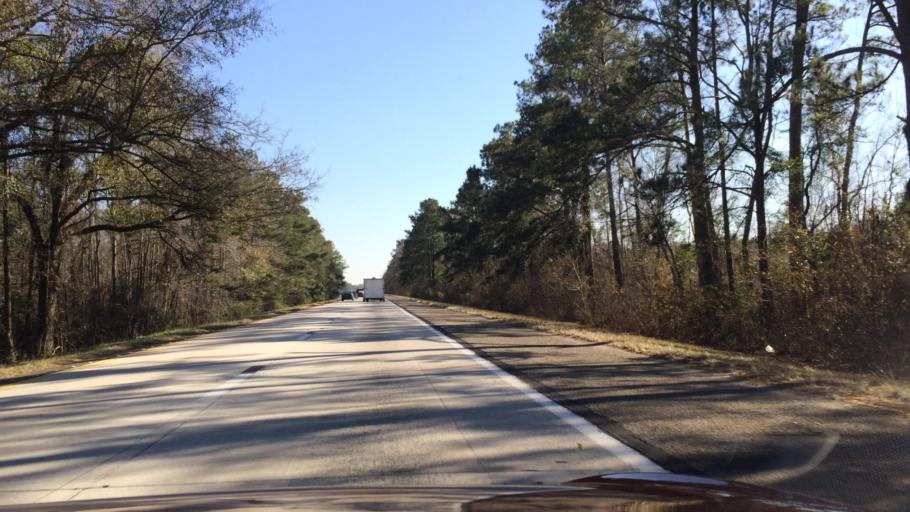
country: US
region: South Carolina
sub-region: Orangeburg County
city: Holly Hill
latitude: 33.2548
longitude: -80.4725
